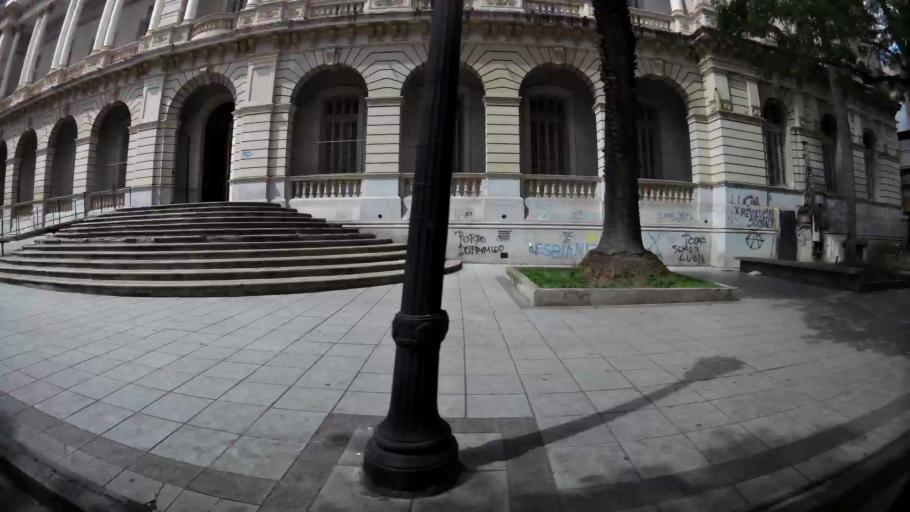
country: AR
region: Santa Fe
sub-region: Departamento de Rosario
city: Rosario
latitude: -32.9429
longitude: -60.6509
